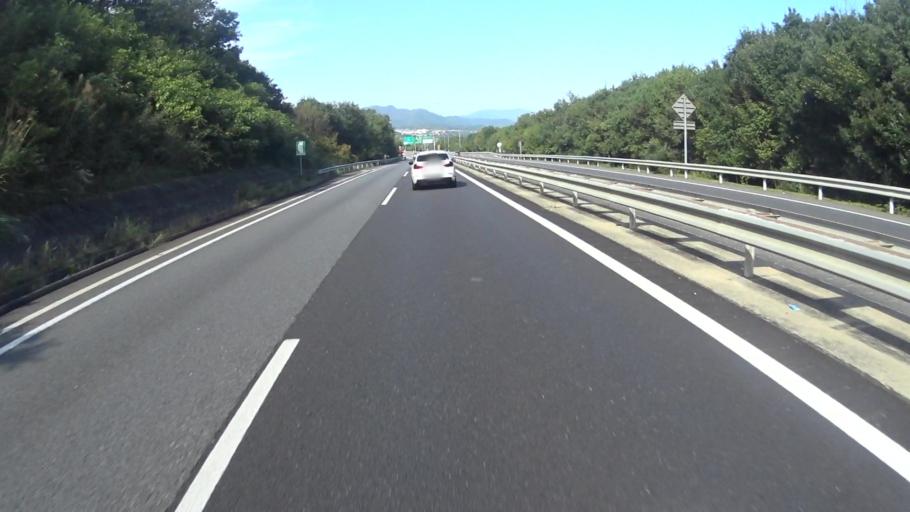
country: JP
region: Kyoto
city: Kameoka
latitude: 34.9903
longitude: 135.6154
